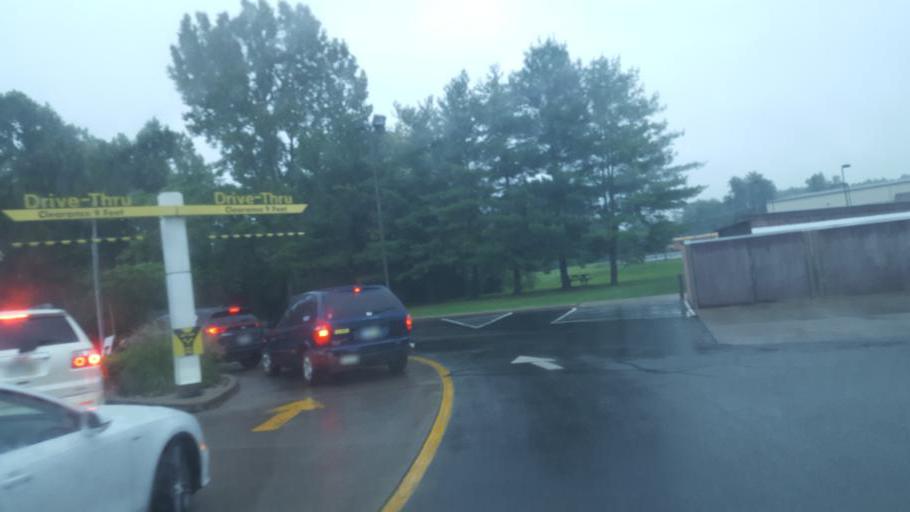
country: US
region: Ohio
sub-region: Jackson County
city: Jackson
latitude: 39.0453
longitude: -82.6296
